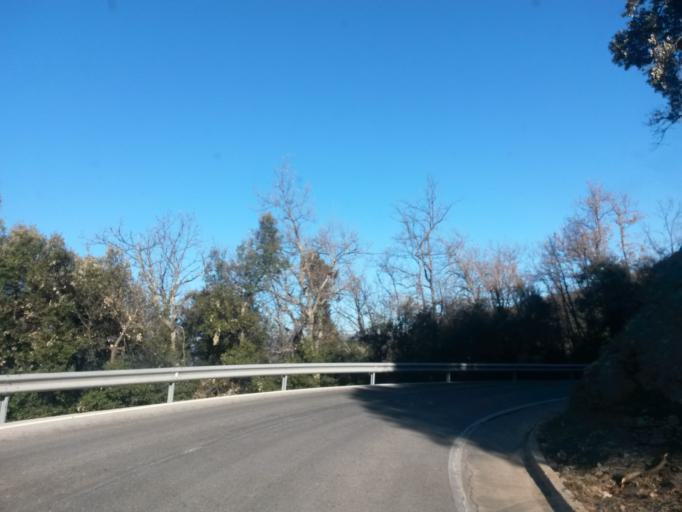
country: ES
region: Catalonia
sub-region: Provincia de Girona
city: Sant Feliu de Pallerols
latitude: 42.0837
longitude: 2.4740
